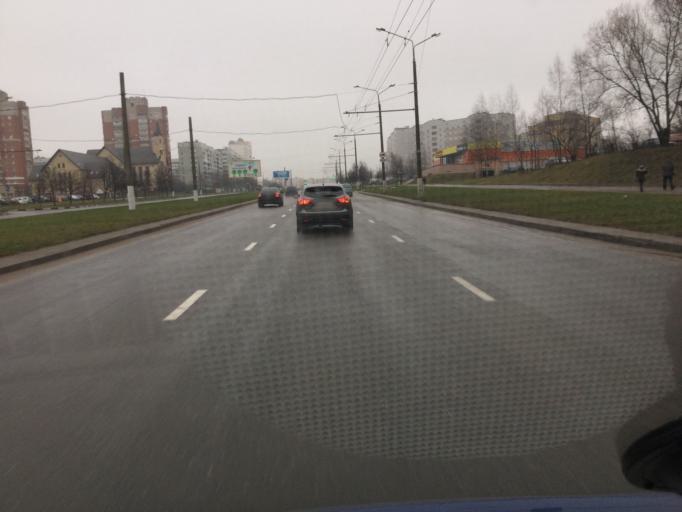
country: BY
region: Vitebsk
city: Vitebsk
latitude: 55.1633
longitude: 30.2112
